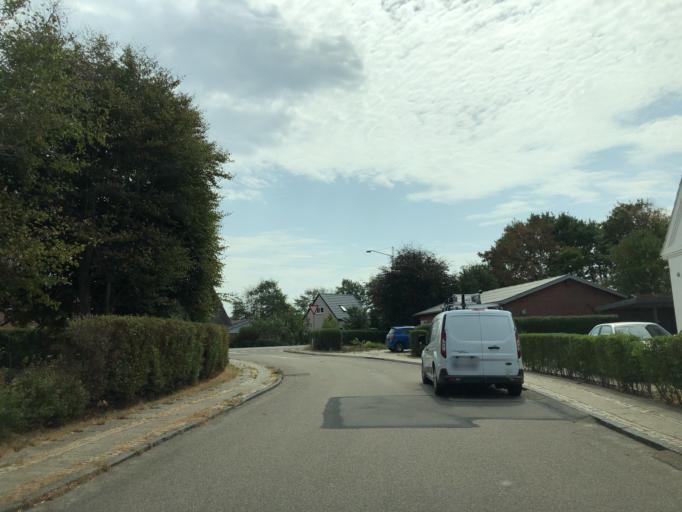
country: DK
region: Central Jutland
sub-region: Ringkobing-Skjern Kommune
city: Tarm
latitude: 55.9001
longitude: 8.5150
